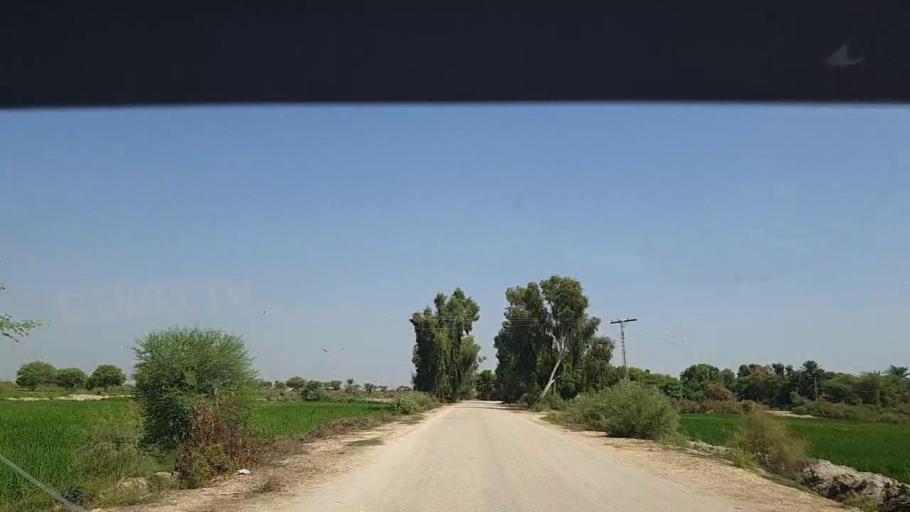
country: PK
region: Sindh
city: Ghauspur
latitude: 28.1567
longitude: 69.1619
